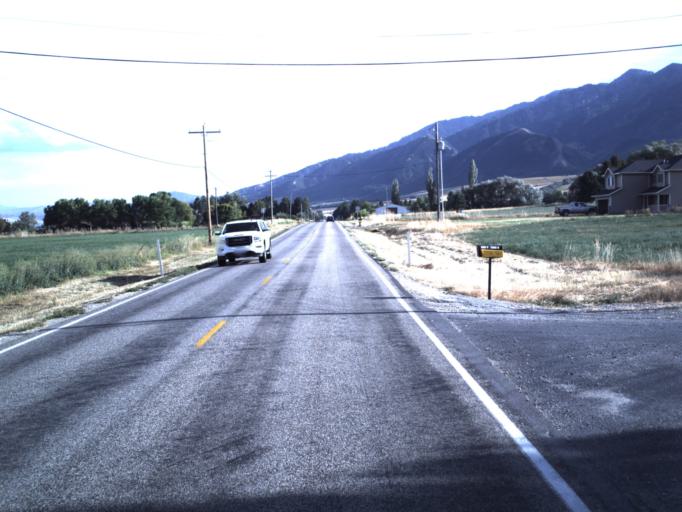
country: US
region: Utah
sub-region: Cache County
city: Mendon
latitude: 41.7250
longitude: -111.9792
